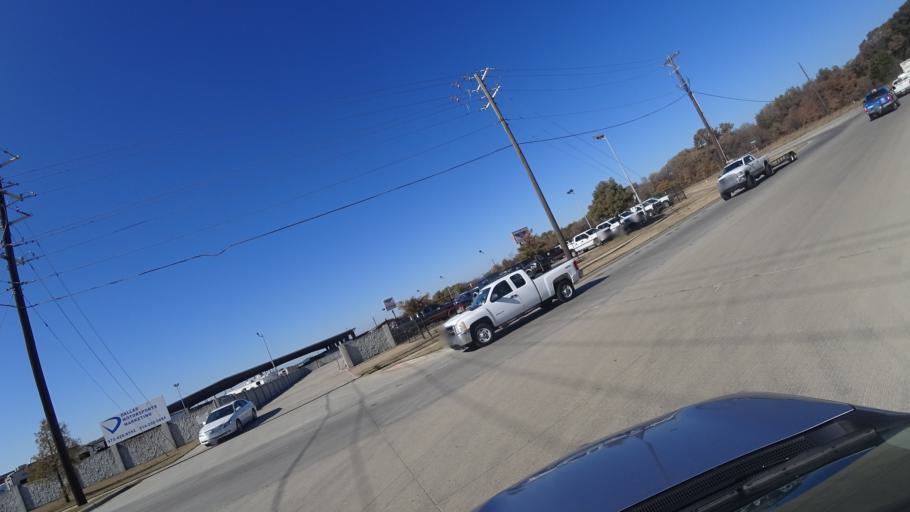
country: US
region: Texas
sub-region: Denton County
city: Lewisville
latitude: 33.0469
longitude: -96.9452
